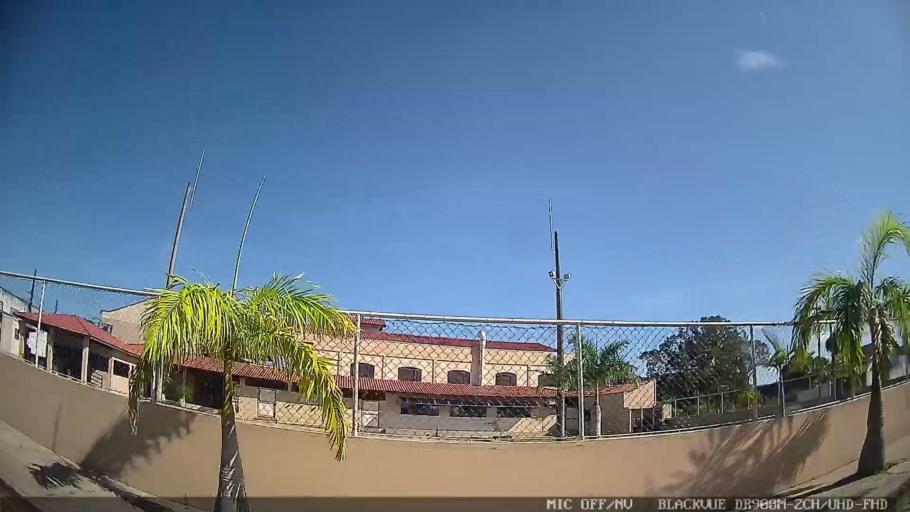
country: BR
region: Sao Paulo
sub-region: Peruibe
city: Peruibe
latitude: -24.2764
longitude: -46.9489
